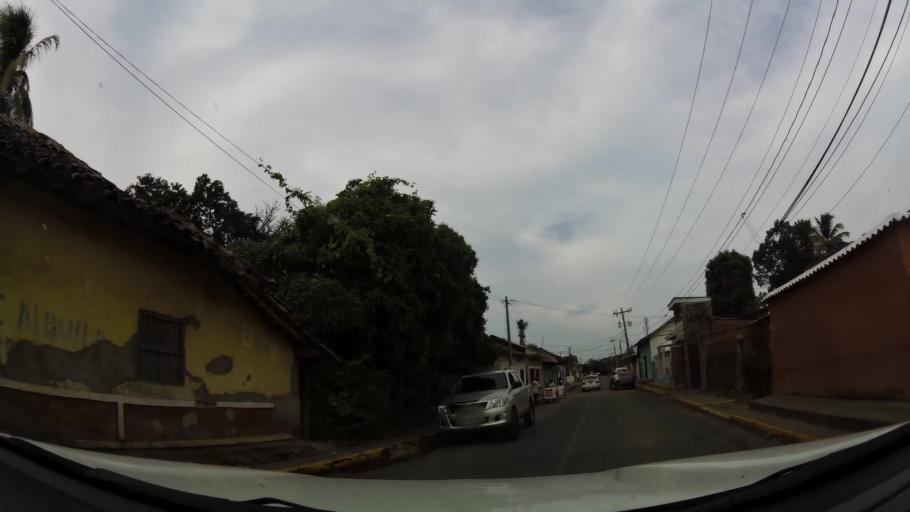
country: NI
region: Rivas
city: San Jorge
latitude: 11.4565
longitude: -85.8005
